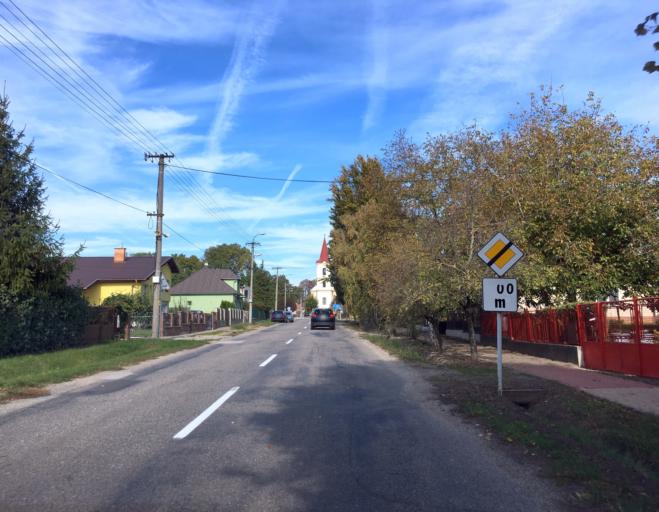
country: SK
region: Nitriansky
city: Svodin
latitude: 48.0155
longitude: 18.4137
